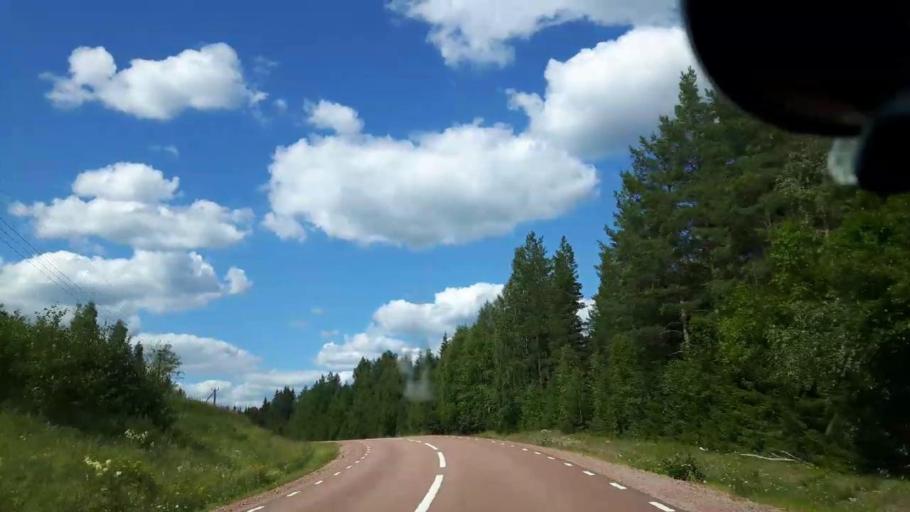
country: SE
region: Jaemtland
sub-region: Ragunda Kommun
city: Hammarstrand
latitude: 63.0156
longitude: 16.6194
